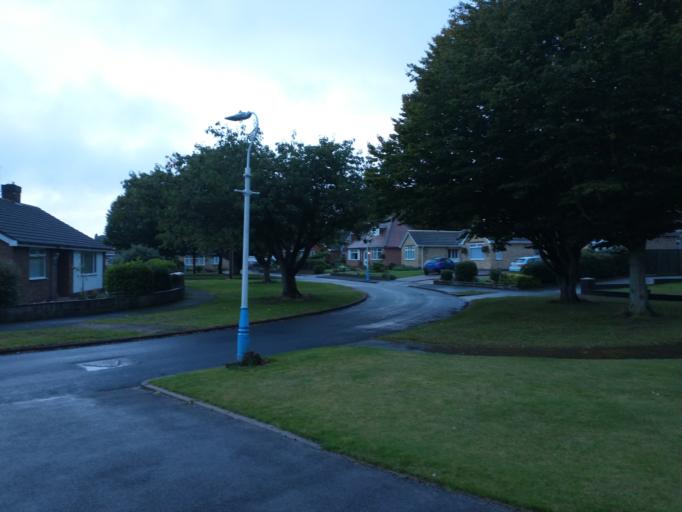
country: GB
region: England
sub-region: East Riding of Yorkshire
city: Kirk Ella
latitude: 53.7470
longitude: -0.4431
